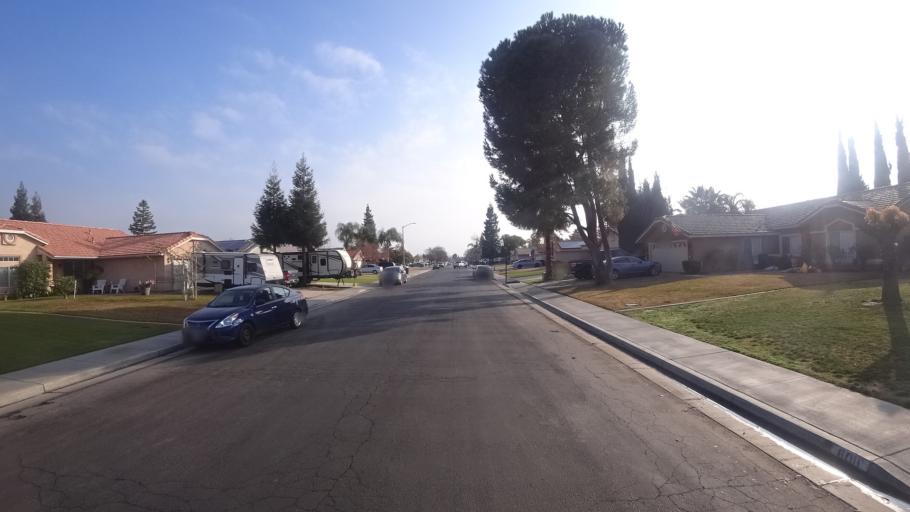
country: US
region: California
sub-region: Kern County
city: Greenfield
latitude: 35.3046
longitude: -119.0692
